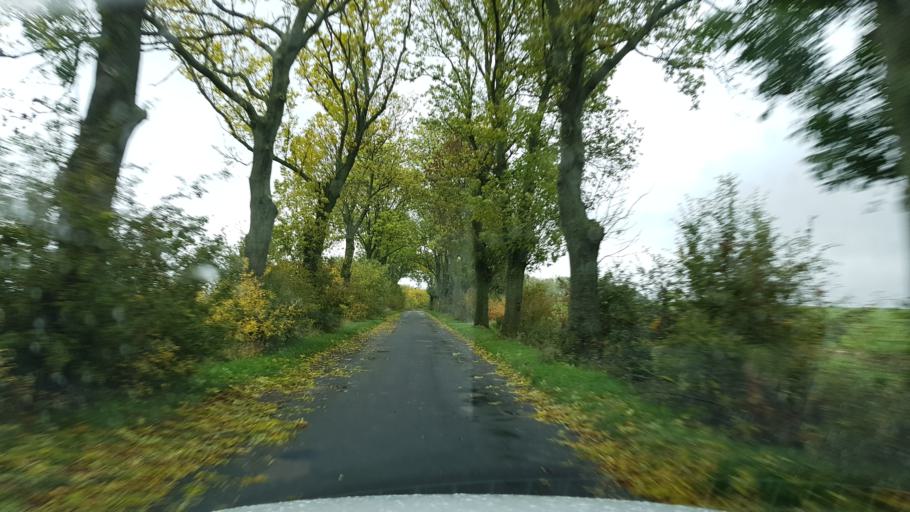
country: PL
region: West Pomeranian Voivodeship
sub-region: Powiat pyrzycki
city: Kozielice
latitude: 53.0601
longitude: 14.8791
